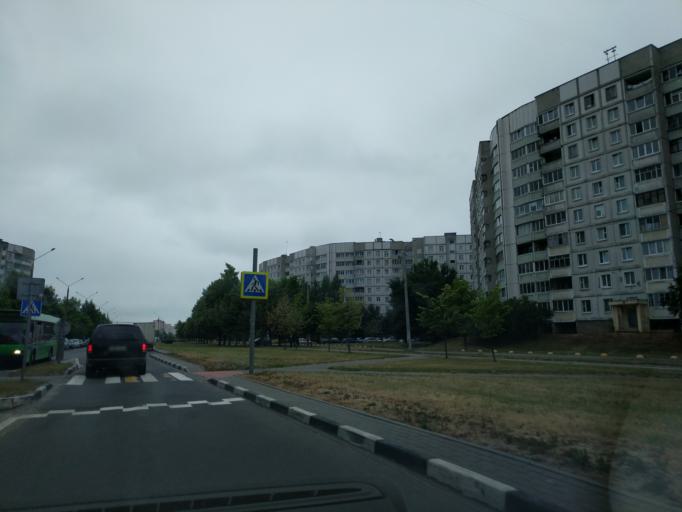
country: BY
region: Minsk
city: Malinovka
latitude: 53.8586
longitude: 27.4601
